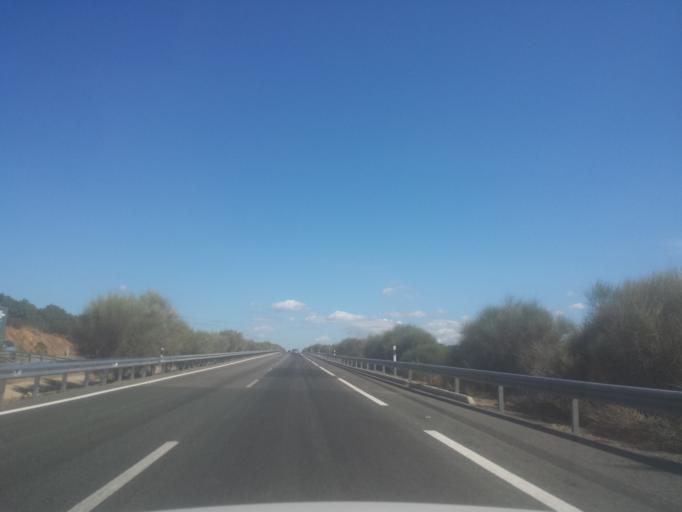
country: ES
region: Andalusia
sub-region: Provincia de Huelva
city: Santa Olalla del Cala
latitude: 37.8649
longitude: -6.2186
